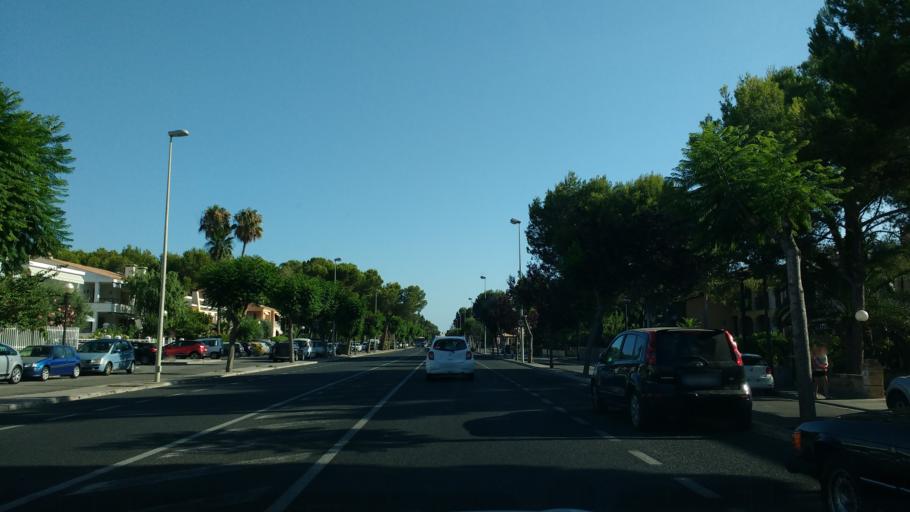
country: ES
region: Balearic Islands
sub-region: Illes Balears
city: Port d'Alcudia
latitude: 39.8241
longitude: 3.1151
